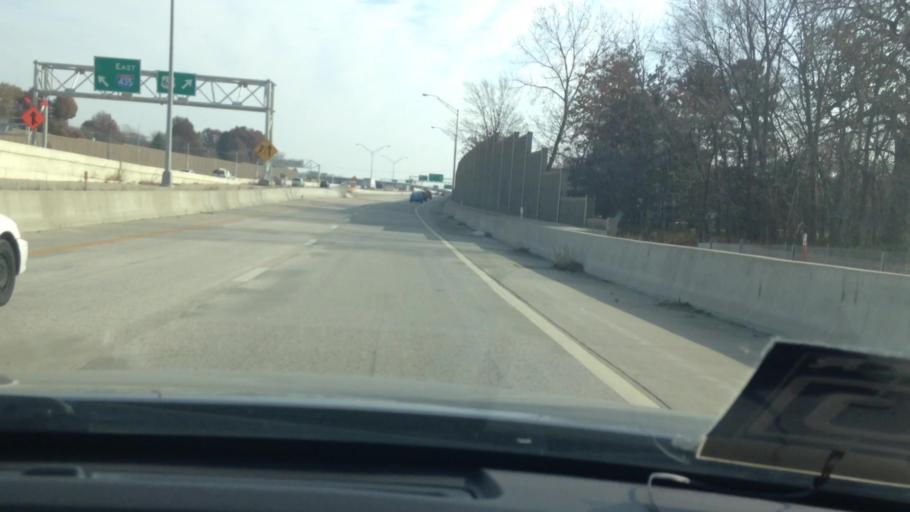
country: US
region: Kansas
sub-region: Johnson County
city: Lenexa
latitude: 38.9348
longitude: -94.7201
